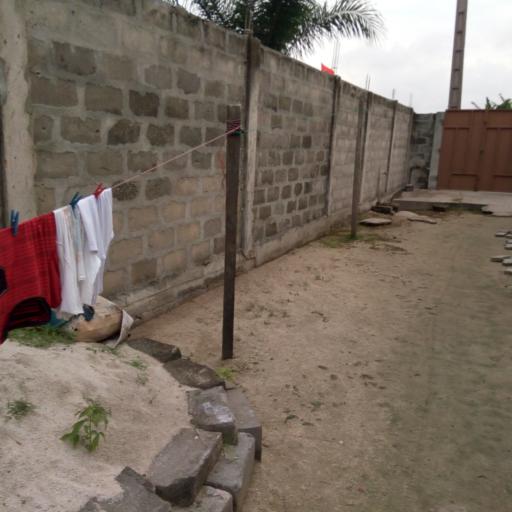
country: BJ
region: Atlantique
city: Abomey-Calavi
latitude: 6.3900
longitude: 2.3614
